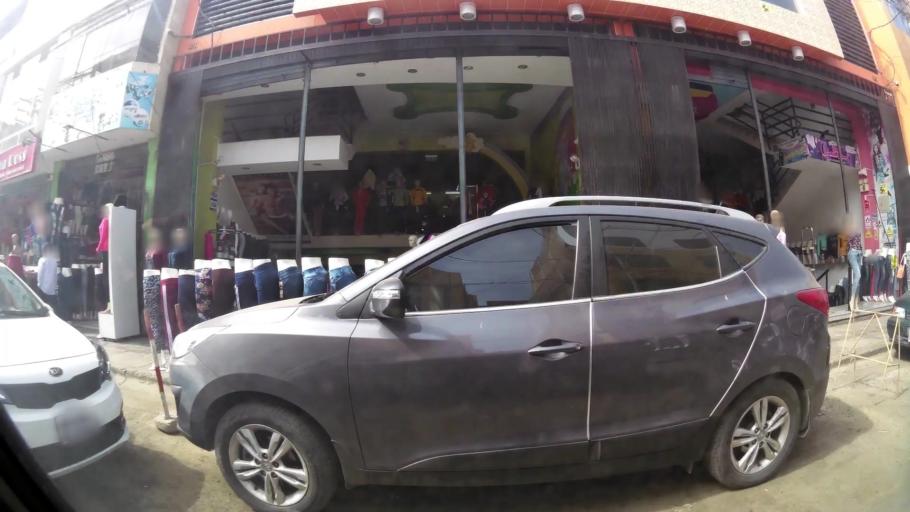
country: PE
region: La Libertad
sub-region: Provincia de Trujillo
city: Trujillo
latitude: -8.1126
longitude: -79.0211
